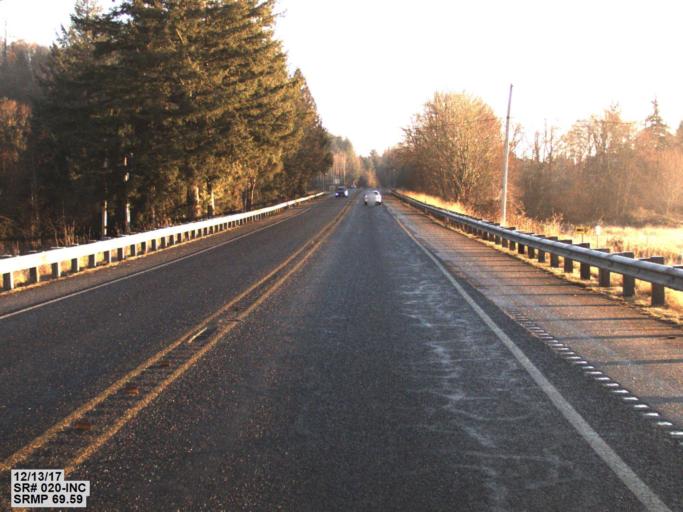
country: US
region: Washington
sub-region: Skagit County
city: Sedro-Woolley
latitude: 48.5294
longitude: -122.1571
